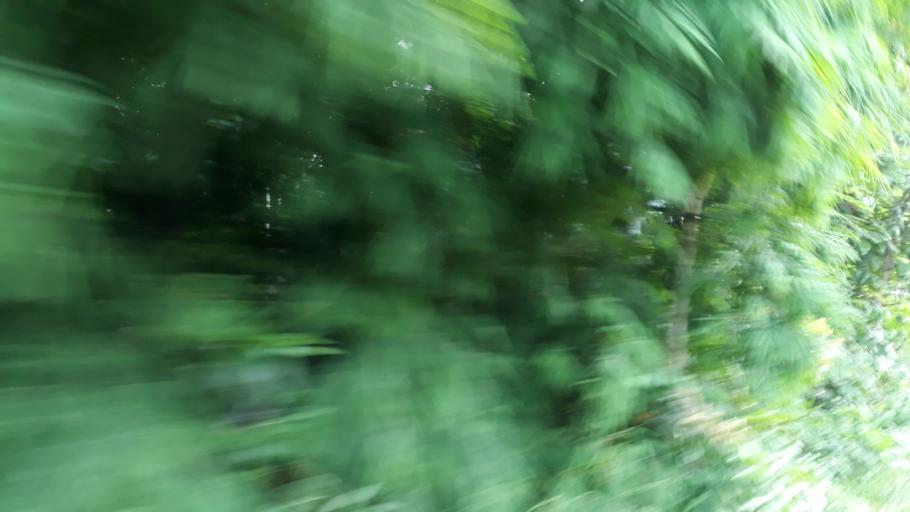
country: LK
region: Western
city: Gampaha
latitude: 7.1013
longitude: 79.9819
